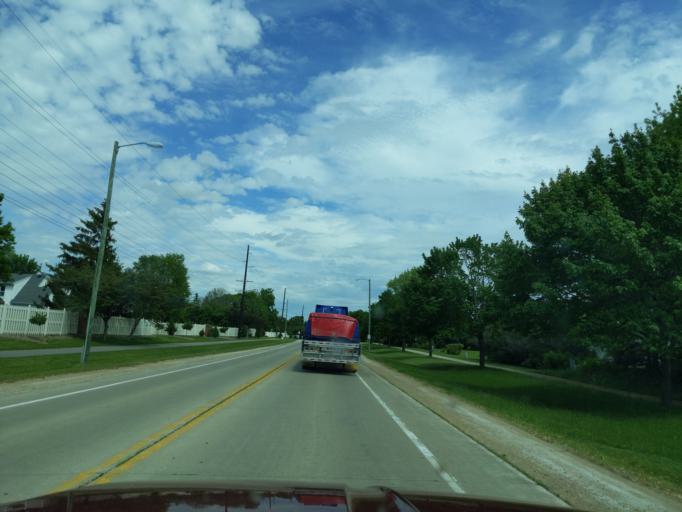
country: US
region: Wisconsin
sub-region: Dane County
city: Sun Prairie
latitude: 43.1873
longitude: -89.2482
